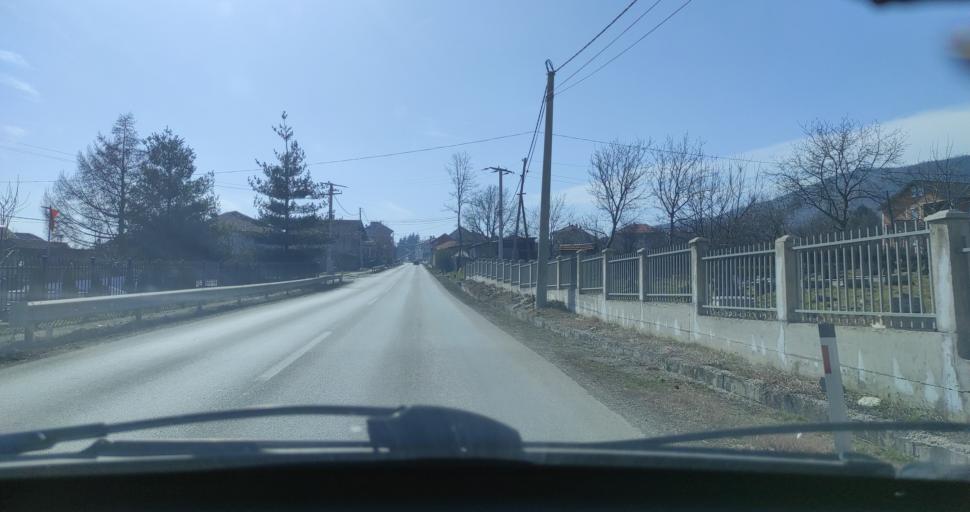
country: XK
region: Gjakova
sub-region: Komuna e Decanit
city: Strellc i Eperm
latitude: 42.5821
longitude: 20.2952
